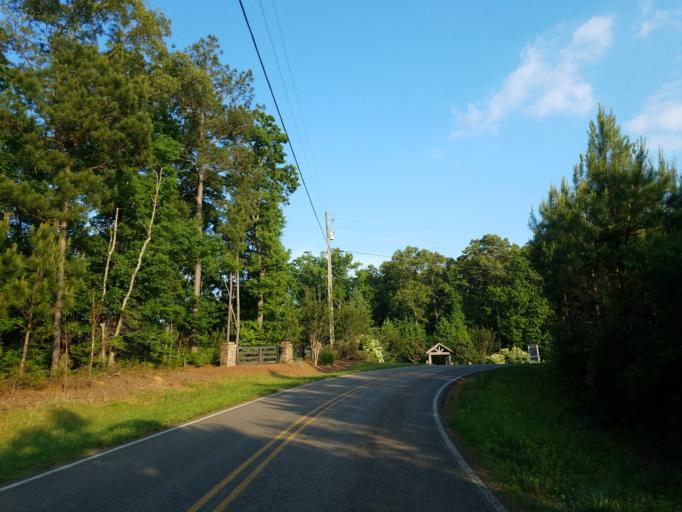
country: US
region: Georgia
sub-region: Cherokee County
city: Ball Ground
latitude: 34.3086
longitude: -84.3653
